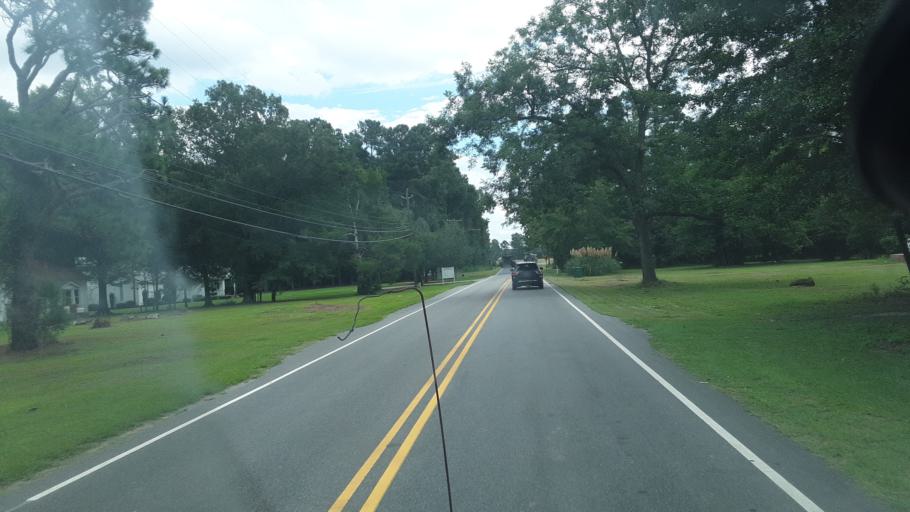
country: US
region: North Carolina
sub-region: Robeson County
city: Rowland
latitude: 34.5333
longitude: -79.2840
